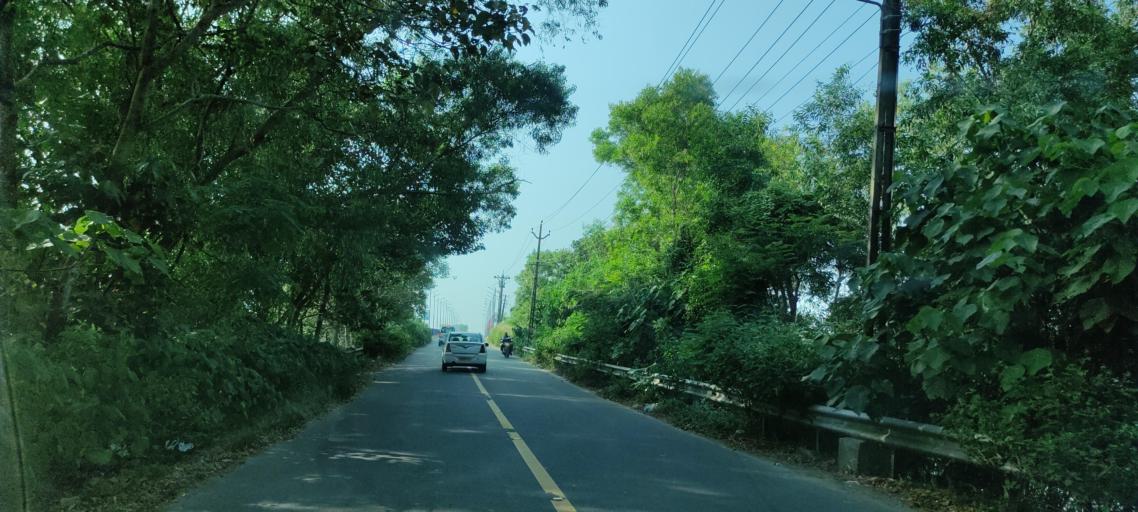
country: IN
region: Kerala
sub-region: Kottayam
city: Changanacheri
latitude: 9.3697
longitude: 76.4263
